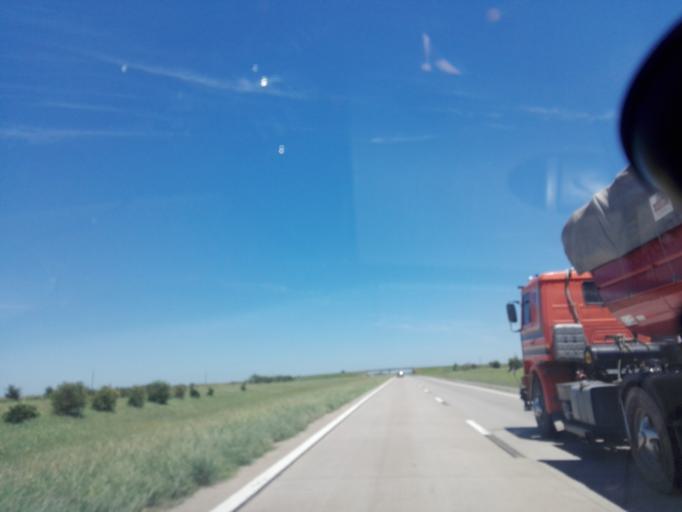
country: AR
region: Santa Fe
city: Armstrong
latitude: -32.8265
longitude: -61.5072
